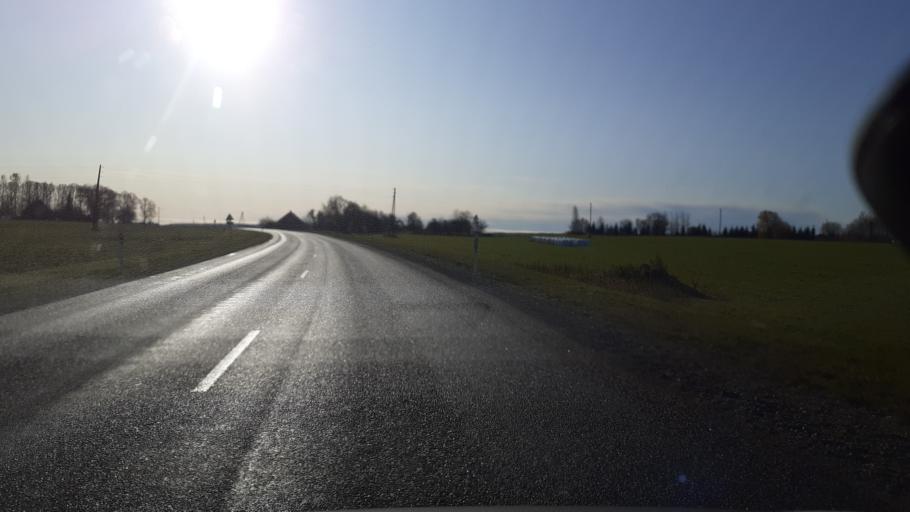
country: LV
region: Kuldigas Rajons
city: Kuldiga
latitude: 57.0140
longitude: 21.8773
